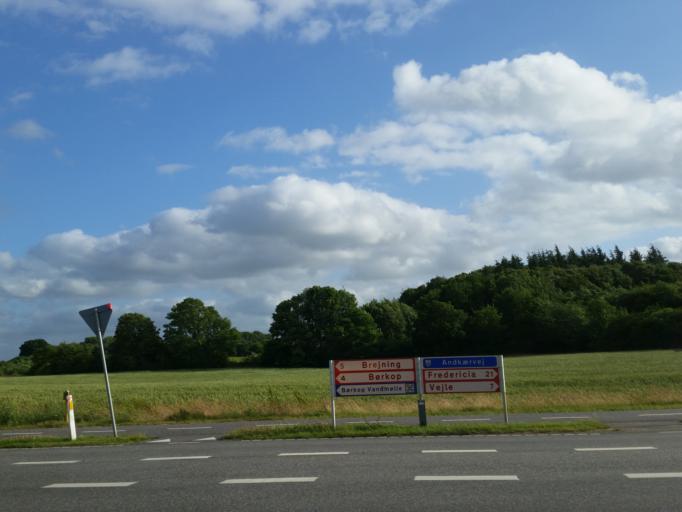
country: DK
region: South Denmark
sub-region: Vejle Kommune
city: Borkop
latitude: 55.6742
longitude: 9.6121
